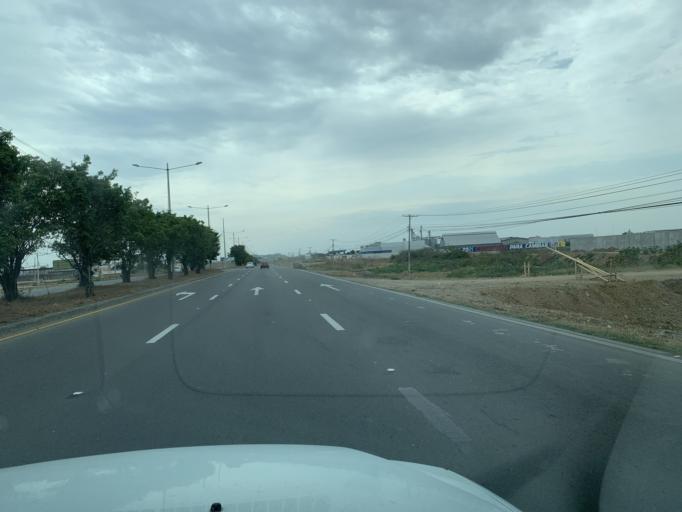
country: EC
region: Guayas
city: Eloy Alfaro
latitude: -2.1874
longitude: -79.8029
